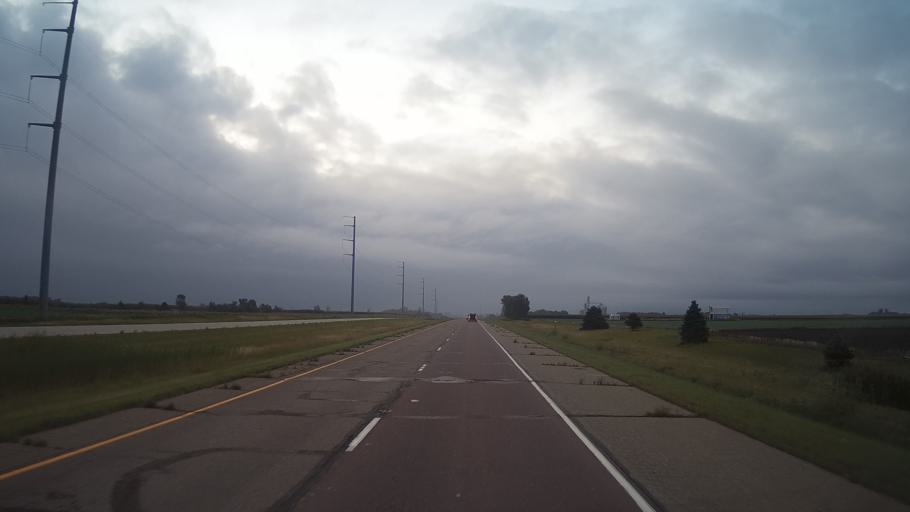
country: US
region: Iowa
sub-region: Dickinson County
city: Lake Park
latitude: 43.6374
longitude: -95.3523
